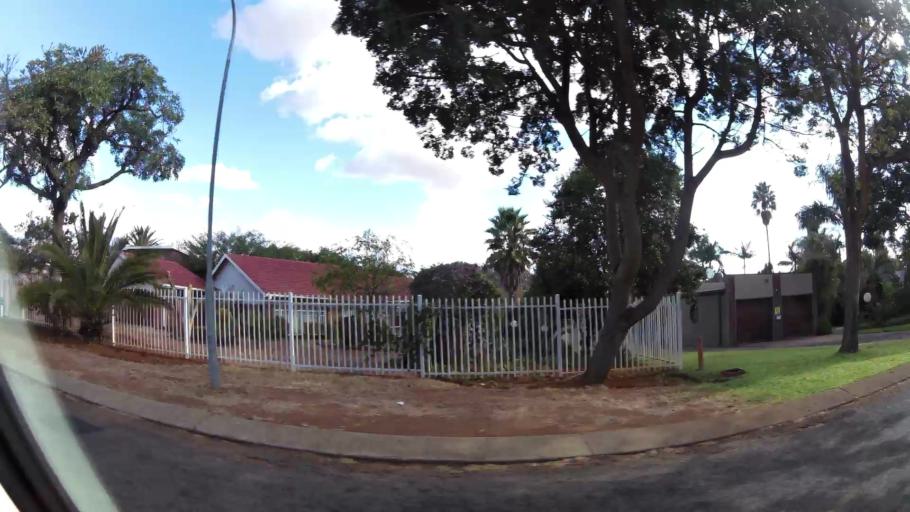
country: ZA
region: Limpopo
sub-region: Capricorn District Municipality
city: Polokwane
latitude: -23.8932
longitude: 29.4818
